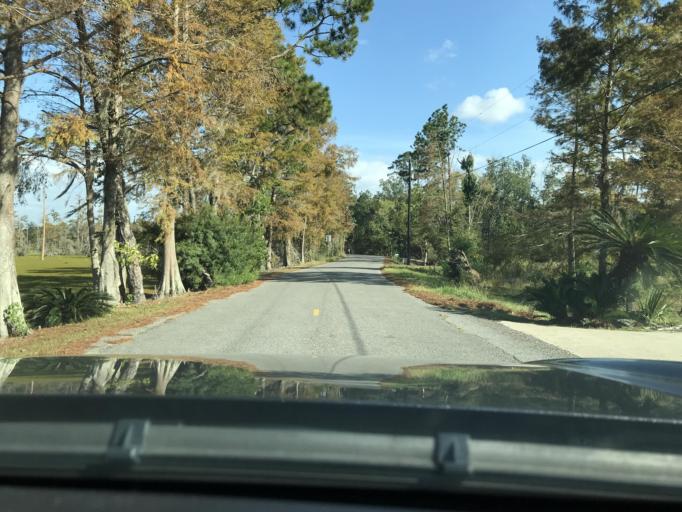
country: US
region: Louisiana
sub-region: Calcasieu Parish
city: Westlake
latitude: 30.3154
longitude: -93.2872
